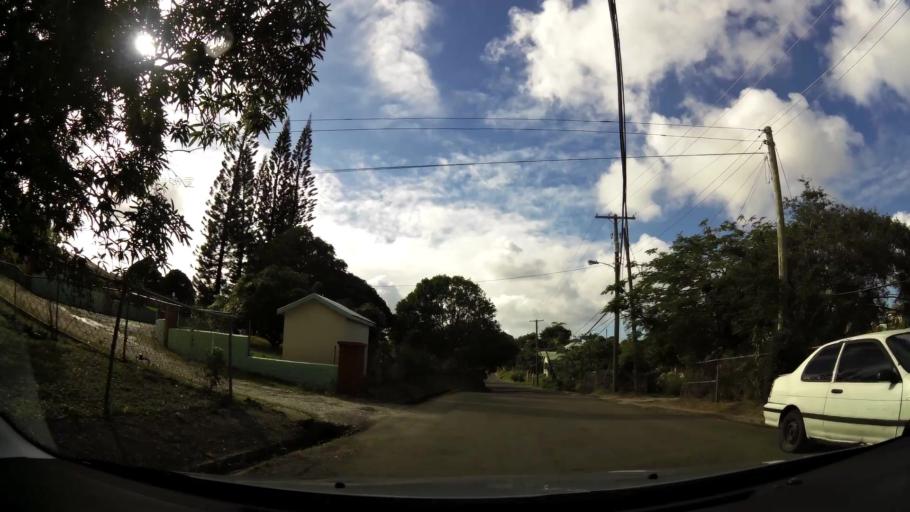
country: AG
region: Saint Peter
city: All Saints
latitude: 17.0506
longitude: -61.7968
